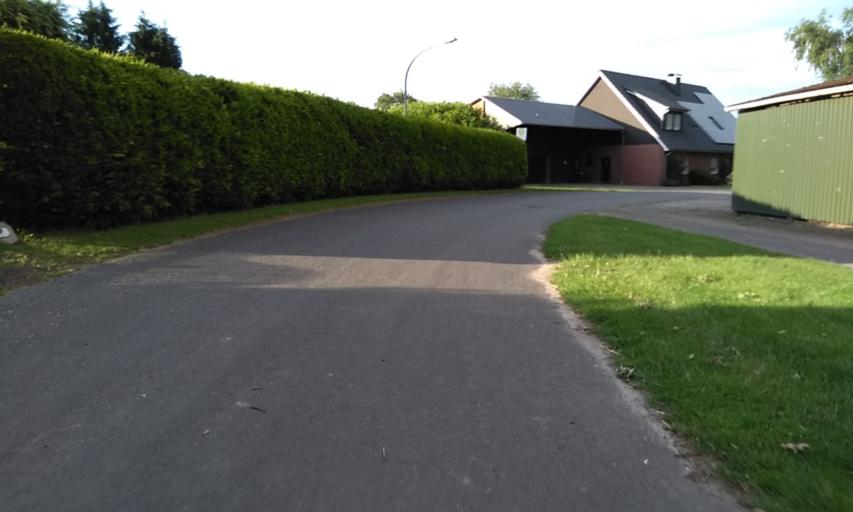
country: DE
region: Lower Saxony
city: Anderlingen
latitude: 53.3867
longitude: 9.3132
